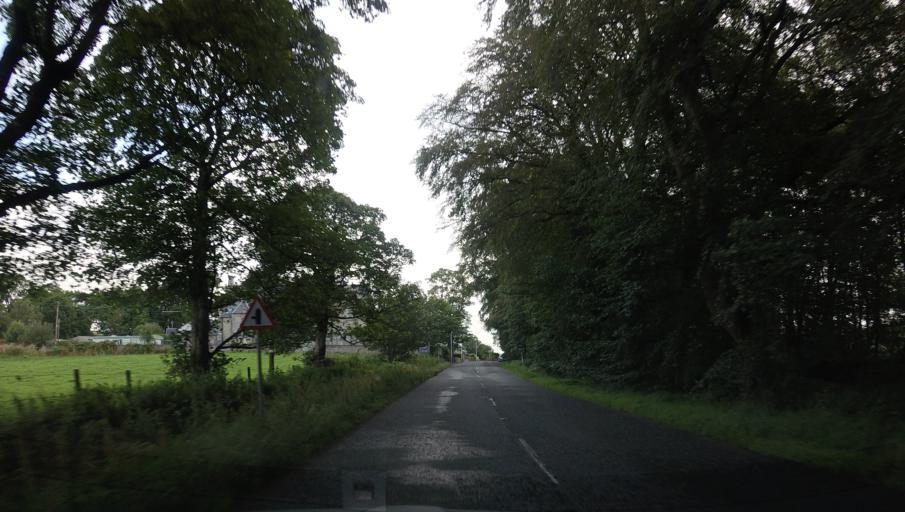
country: GB
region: Scotland
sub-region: Aberdeenshire
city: Westhill
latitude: 57.0765
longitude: -2.3565
